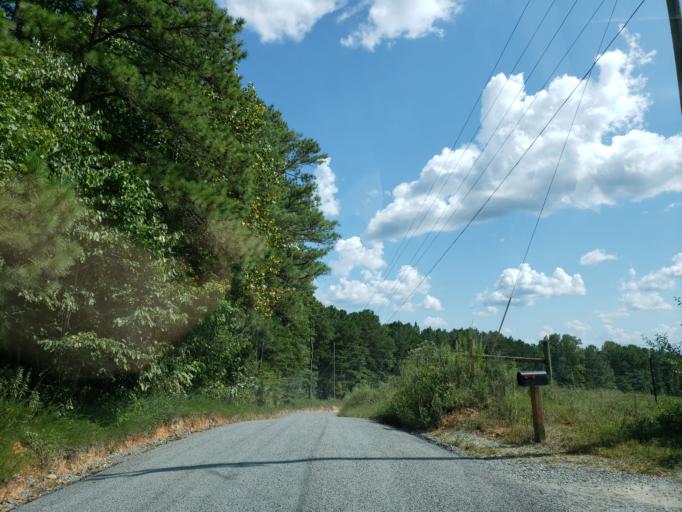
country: US
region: Georgia
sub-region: Pickens County
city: Jasper
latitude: 34.4275
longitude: -84.4553
